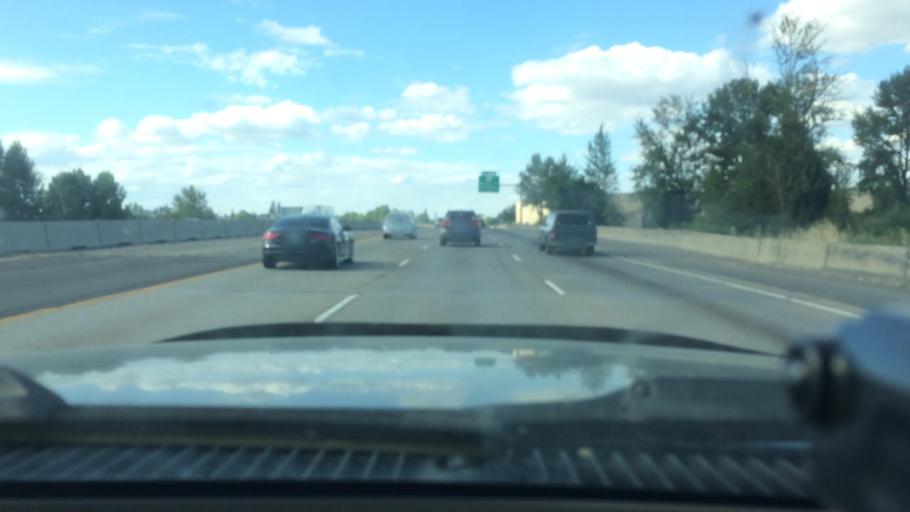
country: US
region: Oregon
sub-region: Marion County
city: Four Corners
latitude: 44.9274
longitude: -122.9902
